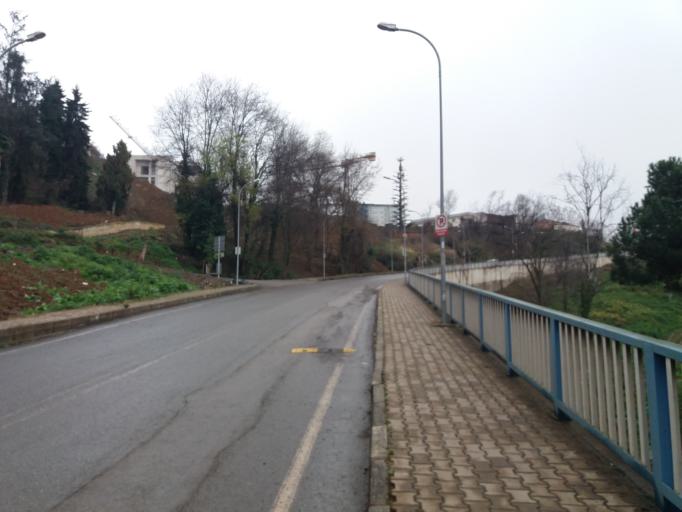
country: TR
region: Trabzon
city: Trabzon
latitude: 40.9914
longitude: 39.7741
